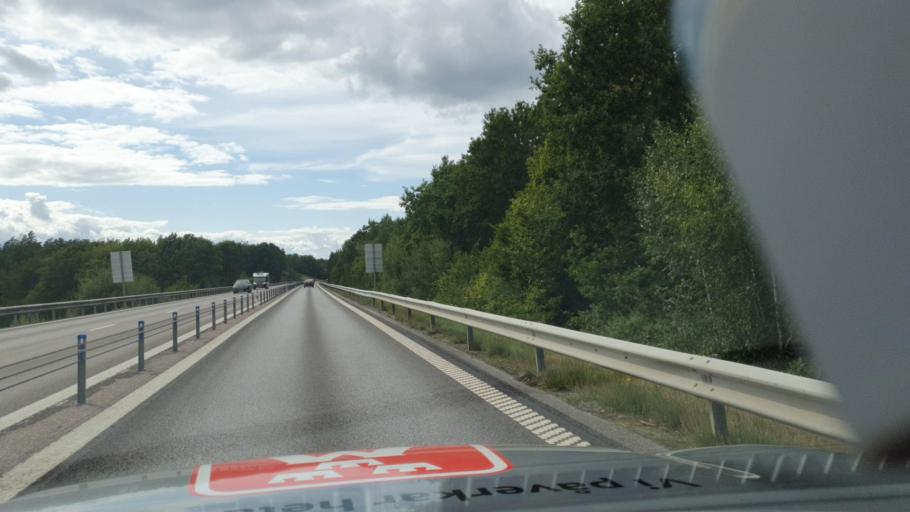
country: SE
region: Blekinge
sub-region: Ronneby Kommun
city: Brakne-Hoby
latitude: 56.2095
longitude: 15.0848
